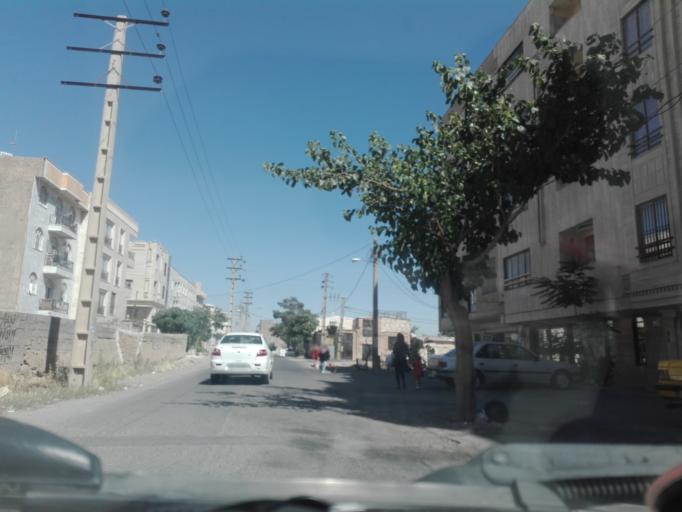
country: IR
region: Tehran
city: Malard
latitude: 35.7201
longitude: 50.9770
